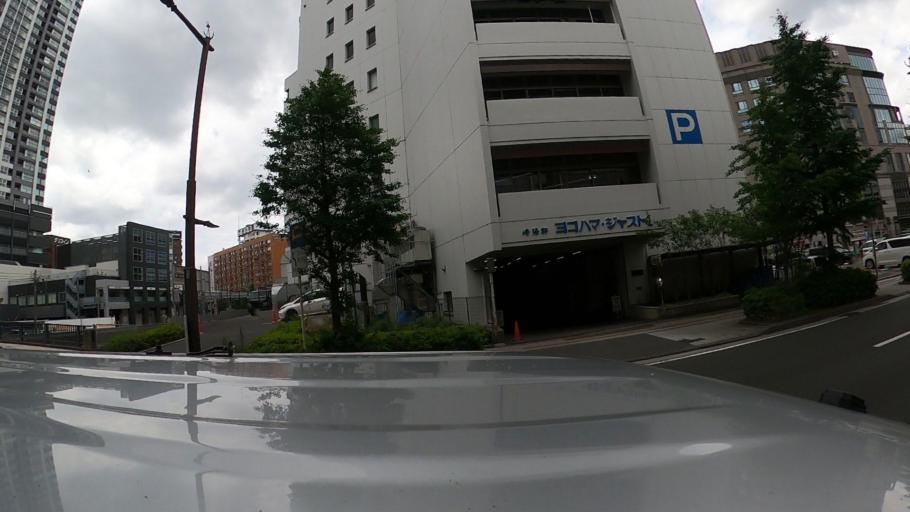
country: JP
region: Kanagawa
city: Yokohama
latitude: 35.4635
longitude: 139.6247
